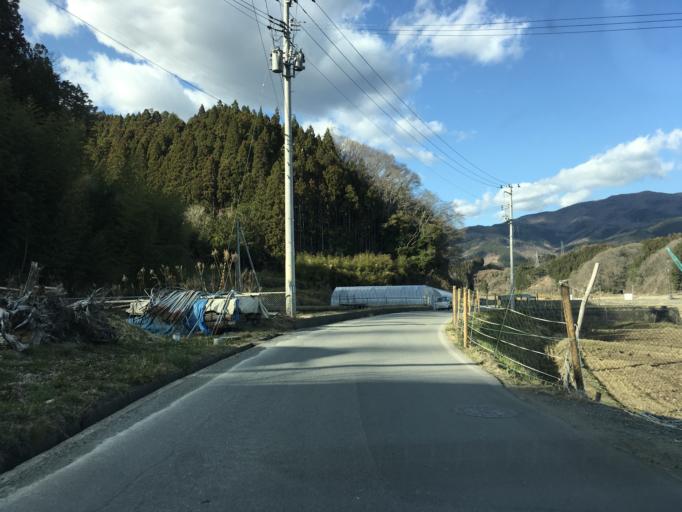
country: JP
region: Iwate
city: Ofunato
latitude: 39.0195
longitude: 141.6149
